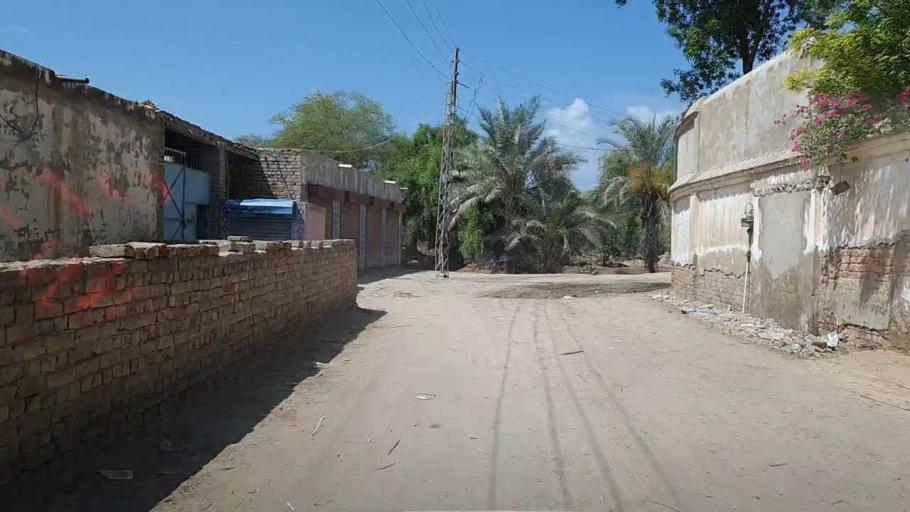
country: PK
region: Sindh
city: Bhiria
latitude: 26.9512
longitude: 68.2314
